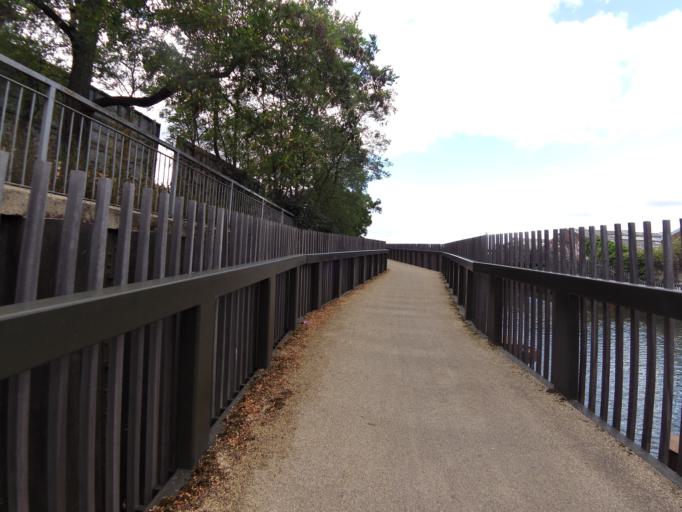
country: GB
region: England
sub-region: Greater London
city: Poplar
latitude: 51.5303
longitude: -0.0144
